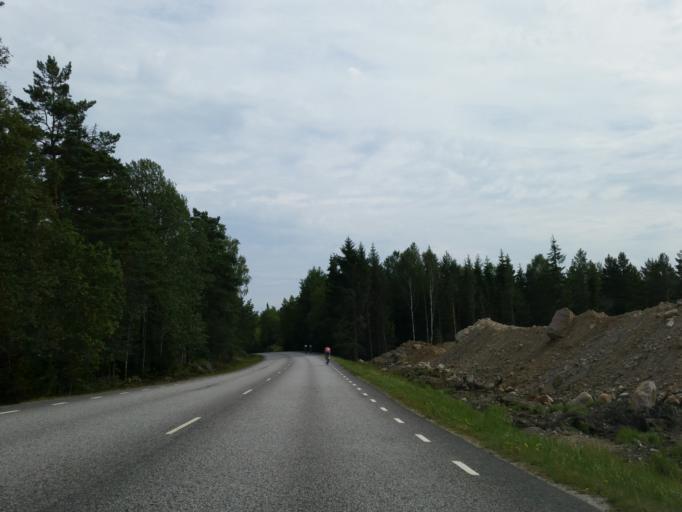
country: SE
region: Soedermanland
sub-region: Strangnas Kommun
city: Mariefred
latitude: 59.2337
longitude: 17.2046
